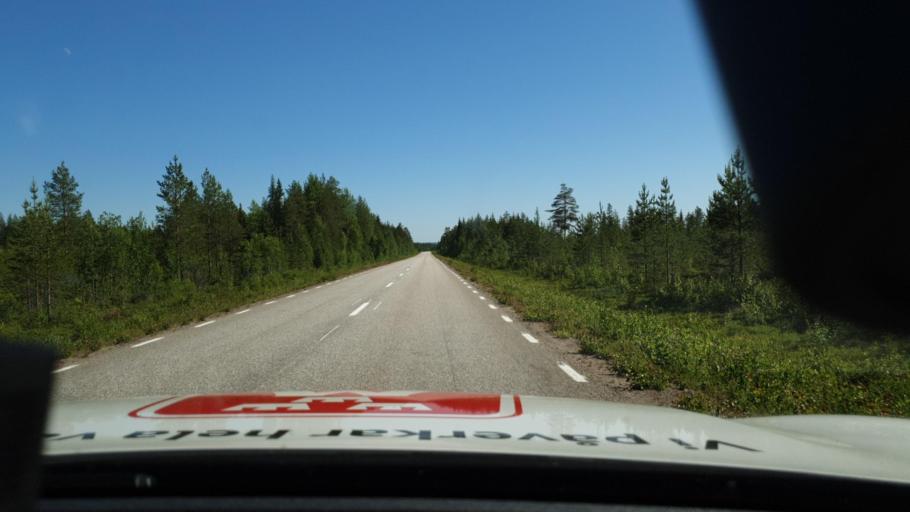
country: SE
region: Norrbotten
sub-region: Lulea Kommun
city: Ranea
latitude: 65.9958
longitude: 22.3358
